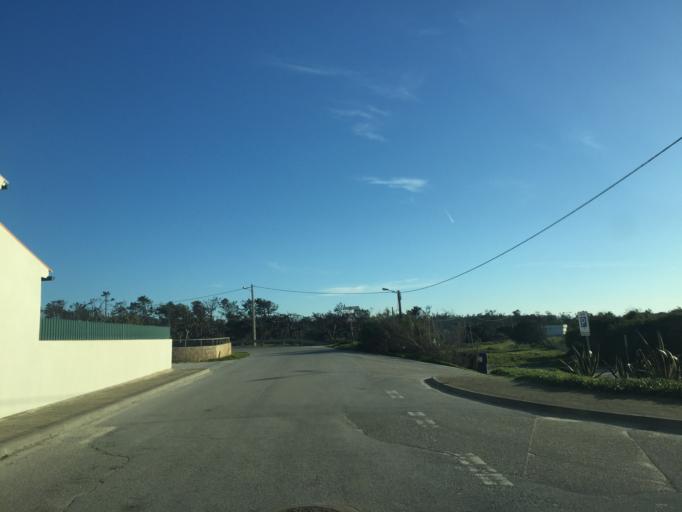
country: PT
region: Coimbra
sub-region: Figueira da Foz
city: Lavos
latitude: 40.0882
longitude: -8.8729
